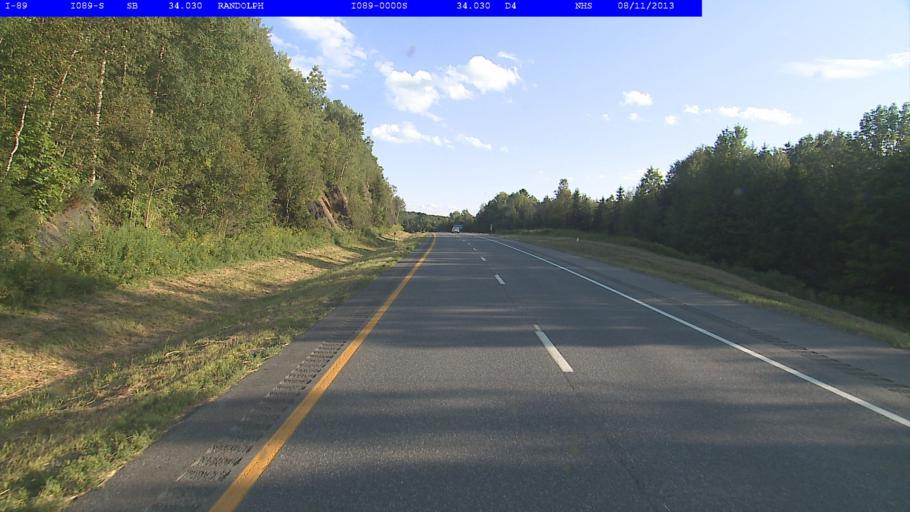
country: US
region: Vermont
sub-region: Orange County
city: Randolph
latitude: 43.9902
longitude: -72.6276
